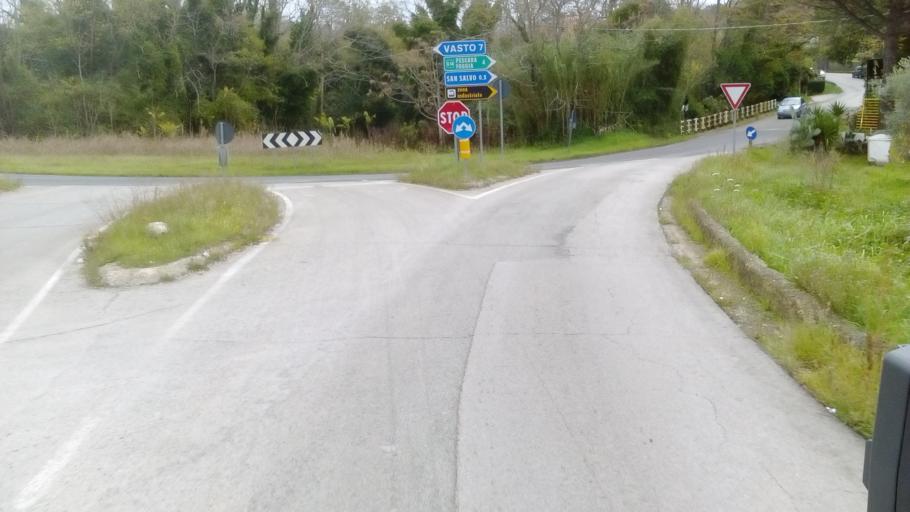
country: IT
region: Abruzzo
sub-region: Provincia di Chieti
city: San Salvo
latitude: 42.0577
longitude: 14.7271
